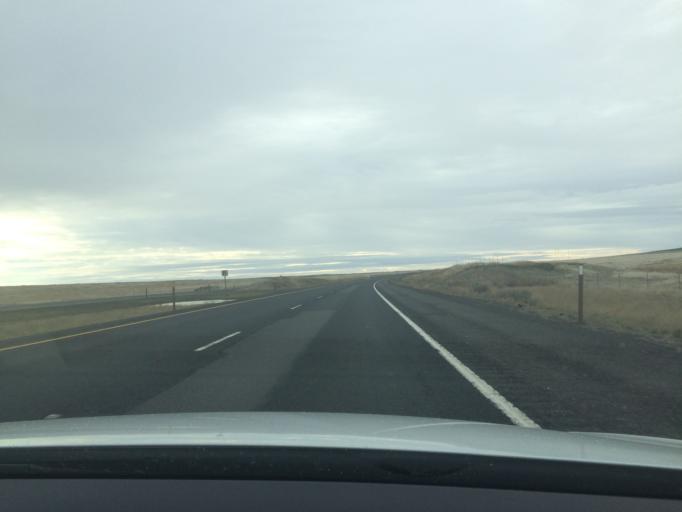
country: US
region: Washington
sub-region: Spokane County
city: Medical Lake
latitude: 47.3401
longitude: -117.9091
